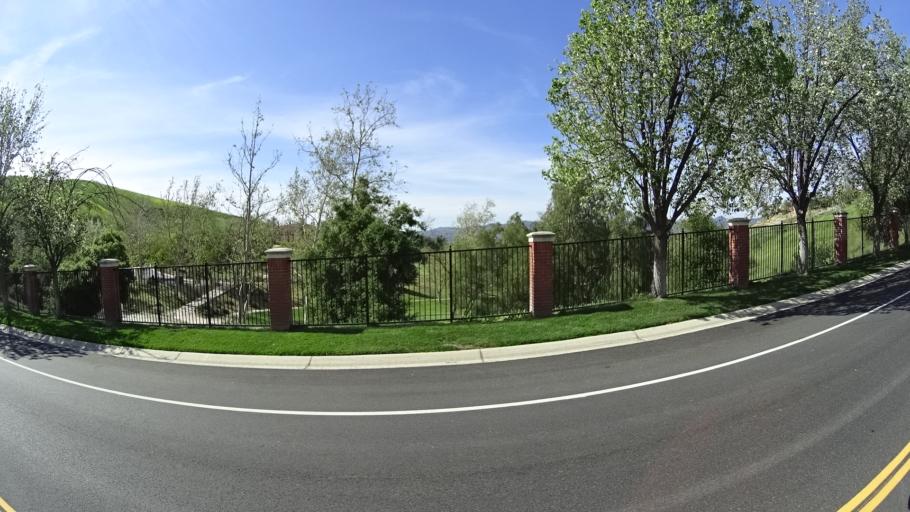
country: US
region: California
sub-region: Ventura County
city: Thousand Oaks
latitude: 34.1886
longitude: -118.8064
